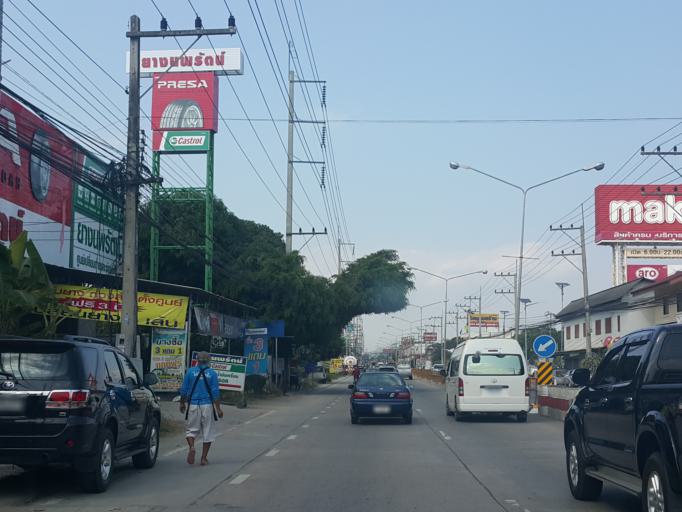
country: TH
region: Chiang Mai
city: San Sai
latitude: 18.8974
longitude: 98.9516
